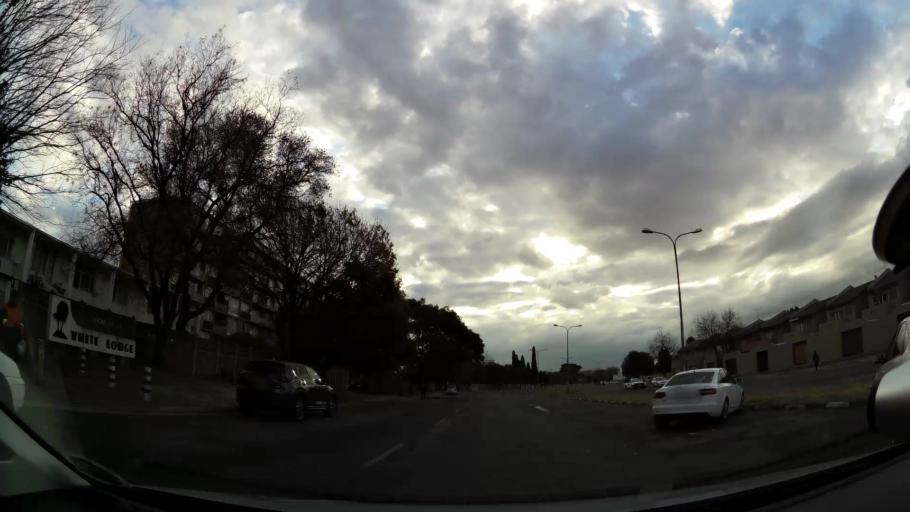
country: ZA
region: Orange Free State
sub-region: Lejweleputswa District Municipality
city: Welkom
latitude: -27.9824
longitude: 26.7316
